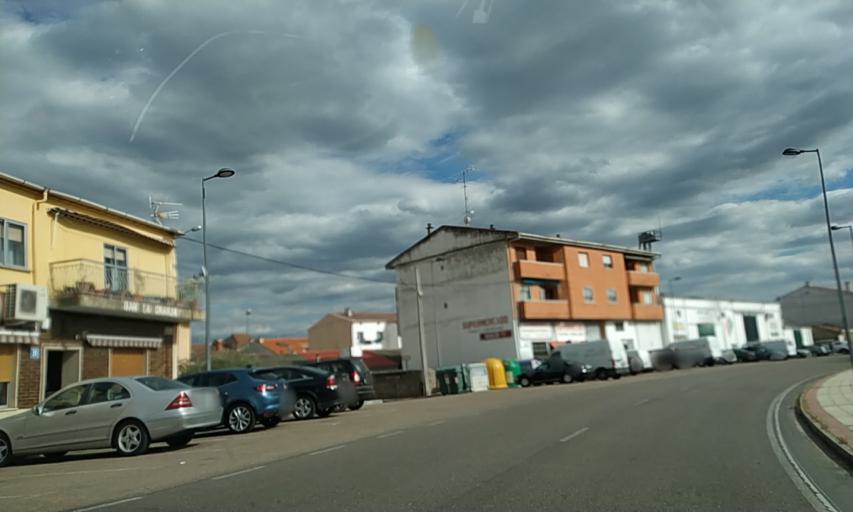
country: ES
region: Castille and Leon
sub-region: Provincia de Salamanca
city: Ciudad Rodrigo
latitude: 40.5909
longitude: -6.5376
